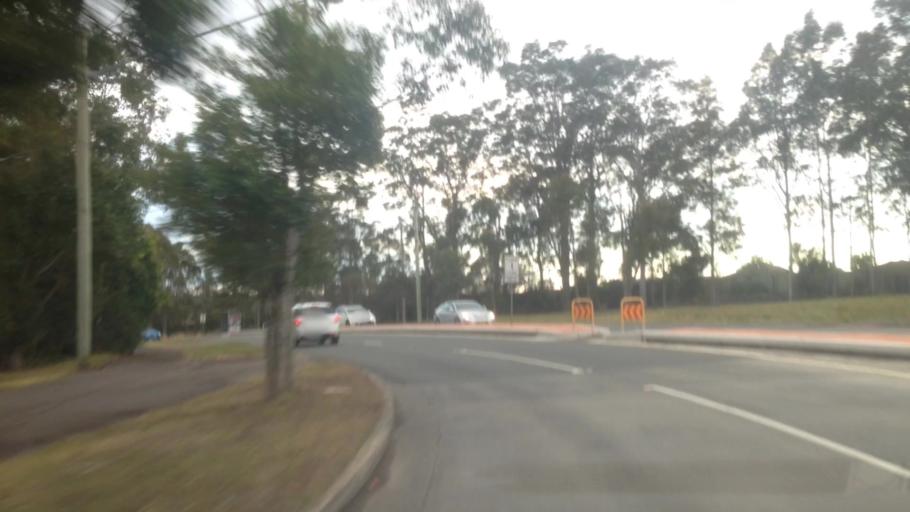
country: AU
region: New South Wales
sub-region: Wyong Shire
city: Tuggerawong
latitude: -33.2708
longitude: 151.4533
